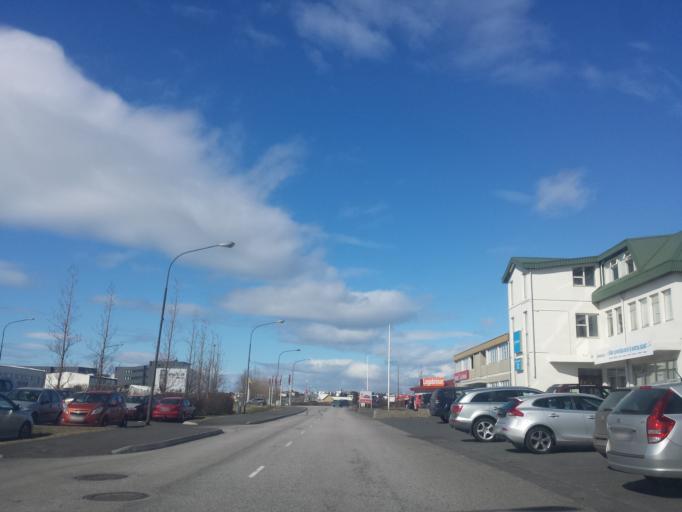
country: IS
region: Capital Region
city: Hafnarfjoerdur
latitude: 64.0801
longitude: -21.9408
